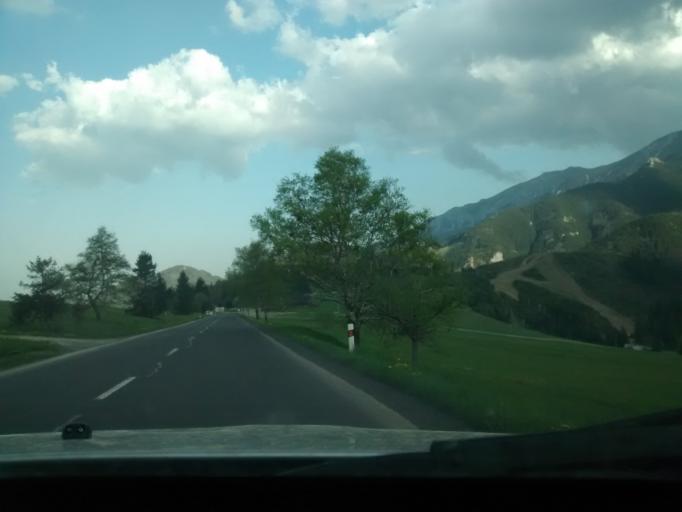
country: SK
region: Presovsky
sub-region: Okres Poprad
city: Zdiar
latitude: 49.2757
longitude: 20.2237
